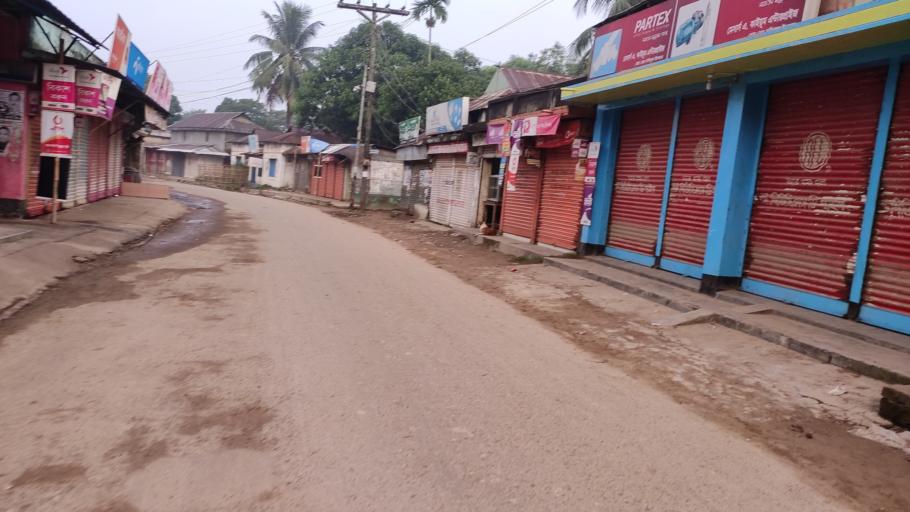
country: BD
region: Dhaka
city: Netrakona
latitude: 24.7167
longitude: 90.9537
